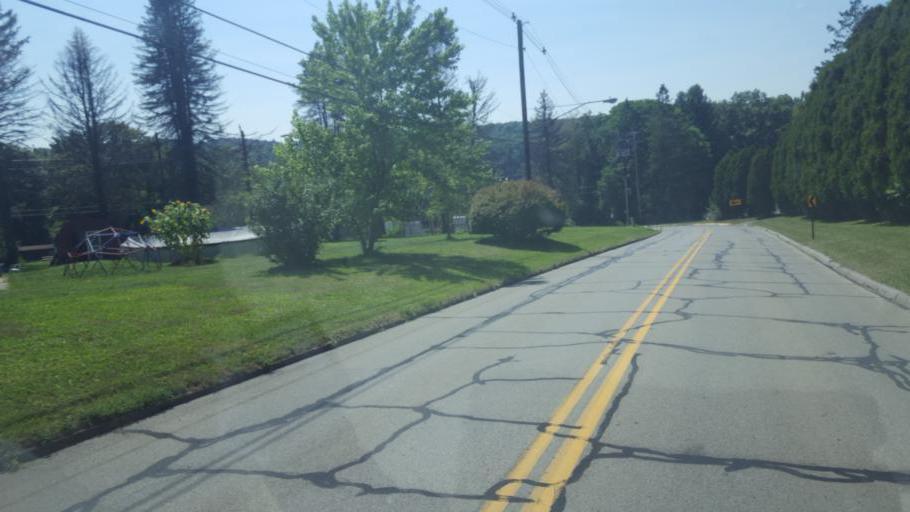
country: US
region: Pennsylvania
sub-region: Clarion County
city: Knox
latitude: 41.1827
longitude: -79.7138
